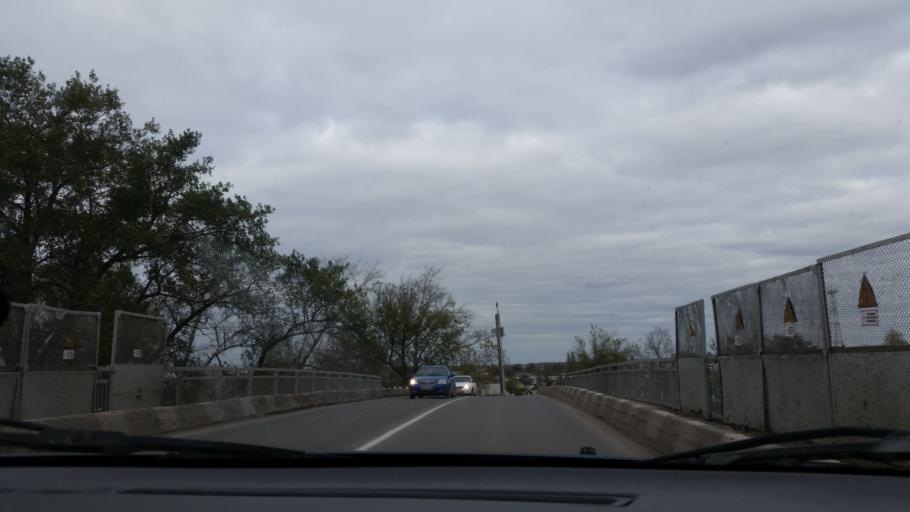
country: RU
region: Lipetsk
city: Gryazi
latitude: 52.4865
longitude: 39.9473
